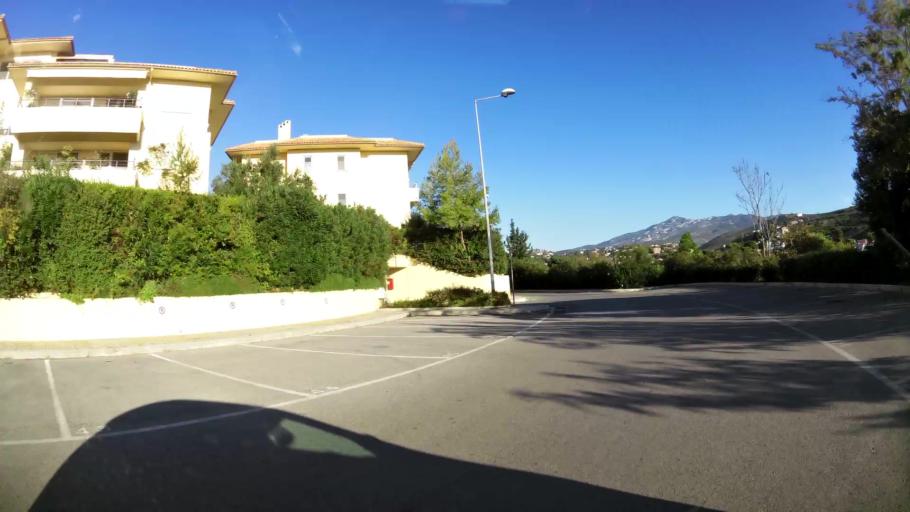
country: GR
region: Attica
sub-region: Nomarchia Anatolikis Attikis
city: Pallini
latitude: 38.0080
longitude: 23.8797
